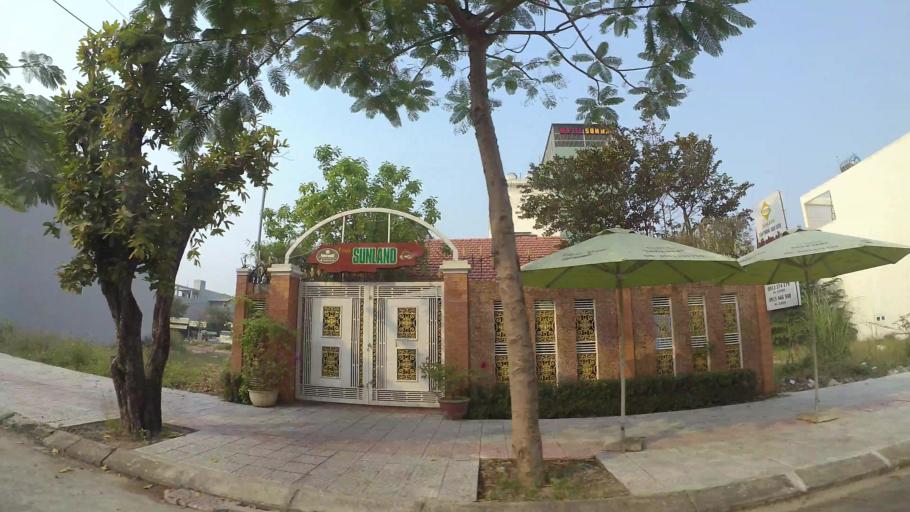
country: VN
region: Da Nang
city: Cam Le
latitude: 16.0111
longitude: 108.2185
